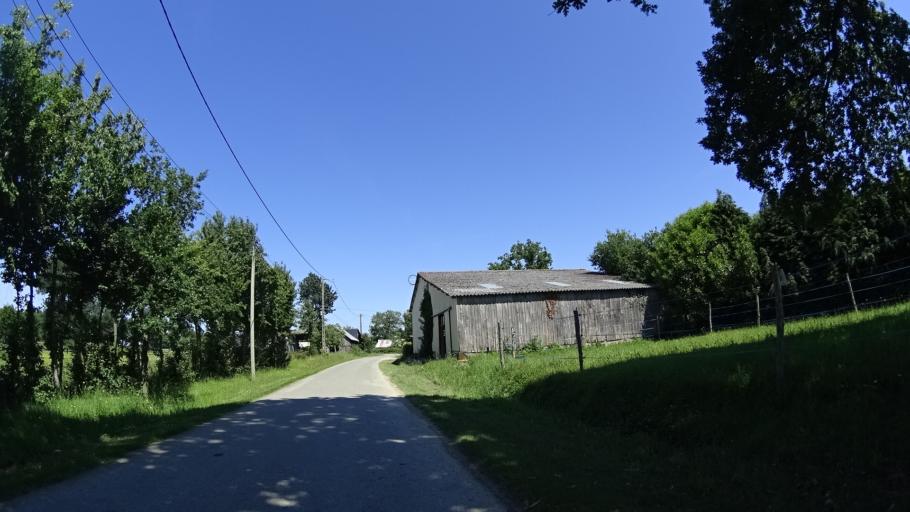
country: FR
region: Brittany
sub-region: Departement d'Ille-et-Vilaine
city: Messac
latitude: 47.7941
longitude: -1.8135
